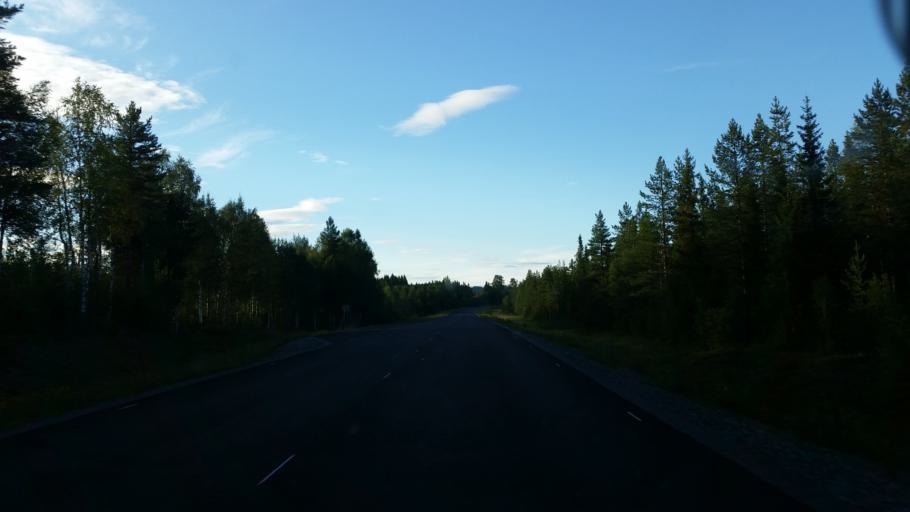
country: SE
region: Vaesterbotten
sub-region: Dorotea Kommun
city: Dorotea
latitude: 64.2780
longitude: 16.5036
